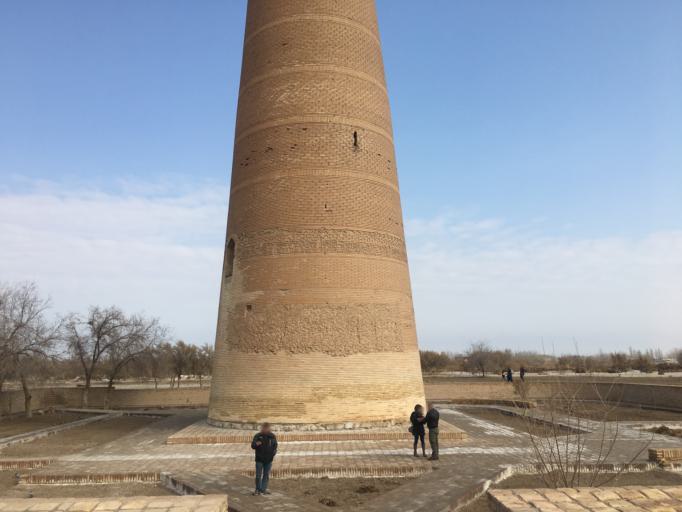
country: TM
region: Dasoguz
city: Koeneuergench
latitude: 42.3083
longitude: 59.1417
